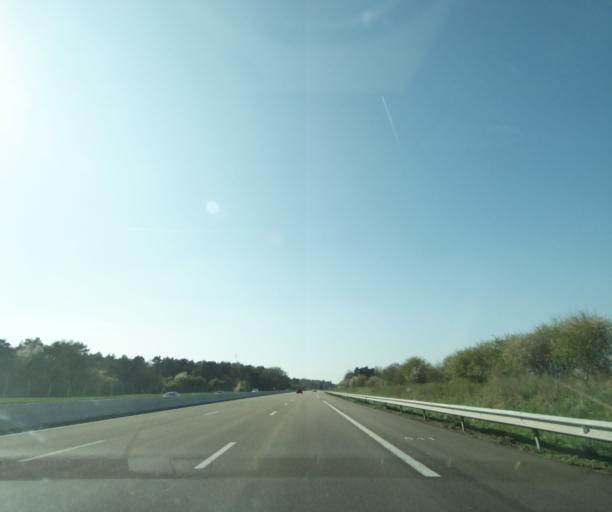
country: FR
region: Ile-de-France
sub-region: Departement de Seine-et-Marne
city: La Chapelle-la-Reine
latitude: 48.3180
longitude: 2.6198
